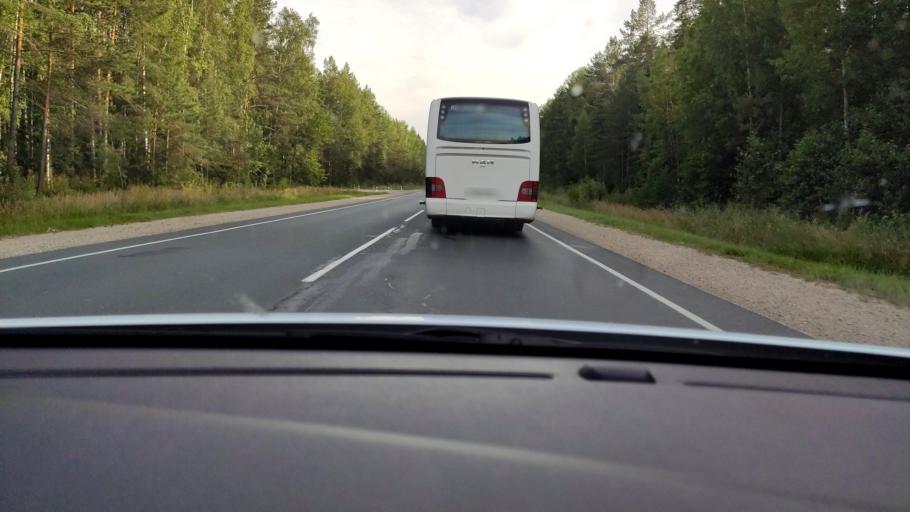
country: RU
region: Mariy-El
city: Suslonger
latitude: 56.3071
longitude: 48.2346
